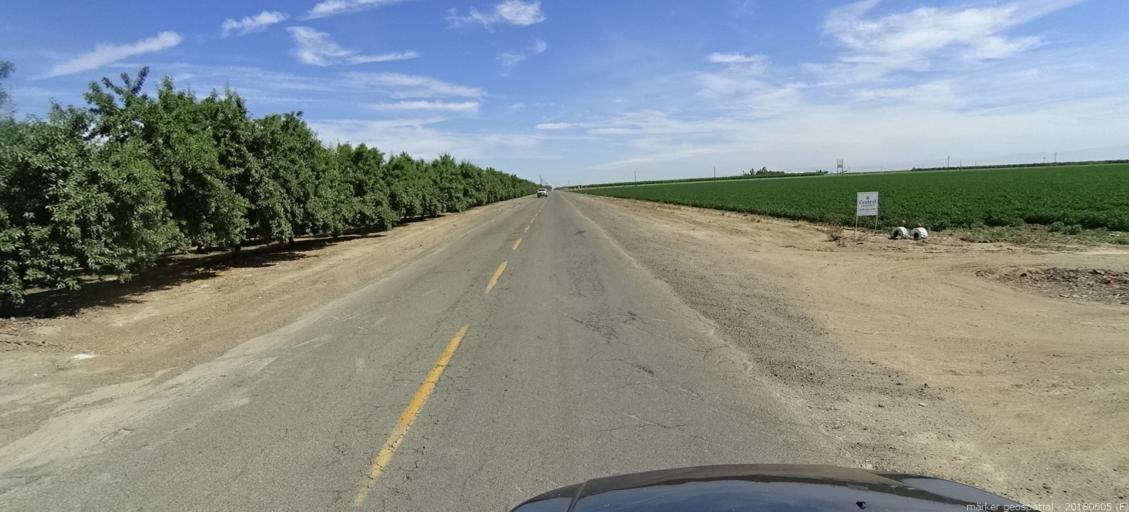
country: US
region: California
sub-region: Madera County
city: Chowchilla
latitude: 37.0288
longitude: -120.3833
